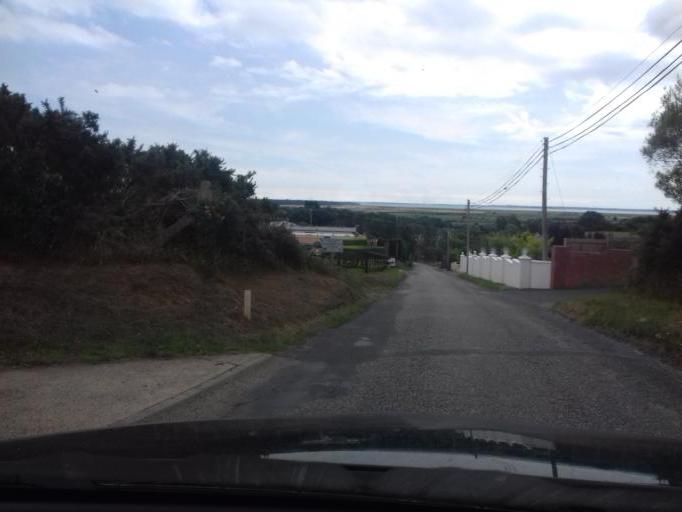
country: IE
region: Leinster
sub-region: Loch Garman
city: Castlebridge
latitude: 52.3970
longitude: -6.3950
